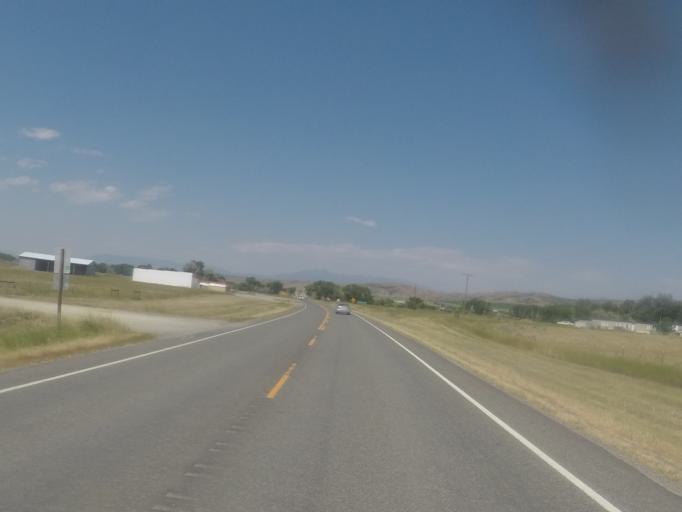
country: US
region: Montana
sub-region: Broadwater County
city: Townsend
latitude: 46.1687
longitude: -111.4497
